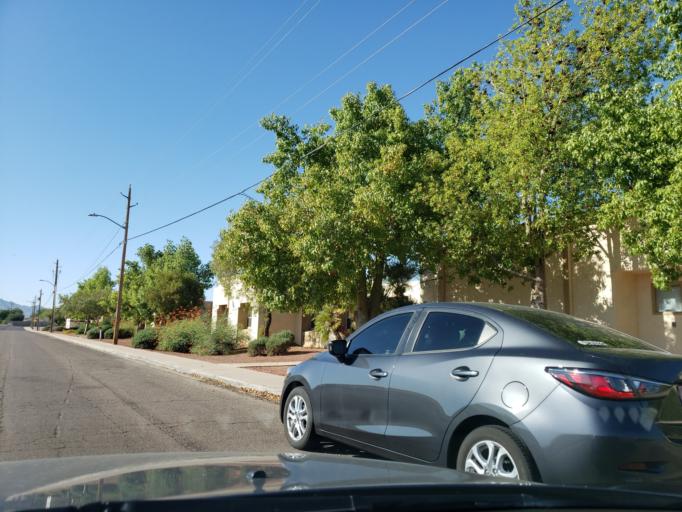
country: US
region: Arizona
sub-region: Maricopa County
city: Avondale
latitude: 33.4478
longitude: -112.3454
